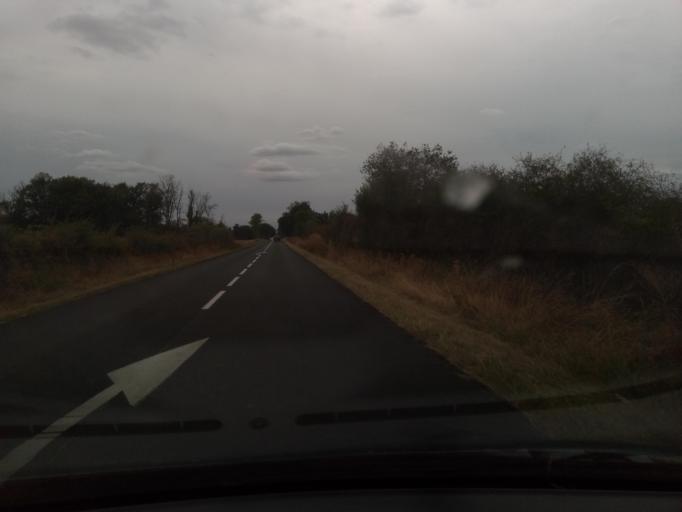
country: FR
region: Poitou-Charentes
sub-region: Departement de la Vienne
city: Pleumartin
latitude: 46.6493
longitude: 0.7676
